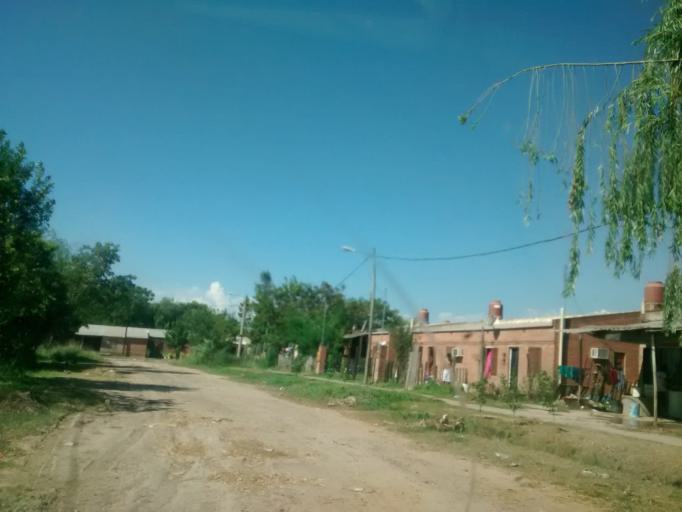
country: AR
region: Chaco
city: Fontana
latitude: -27.4021
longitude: -58.9923
